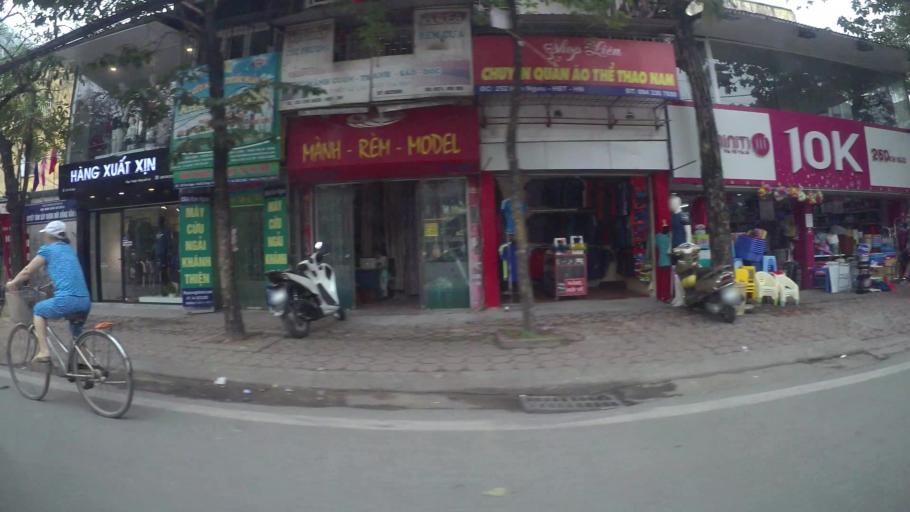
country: VN
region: Ha Noi
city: Hai BaTrung
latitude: 21.0001
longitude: 105.8616
